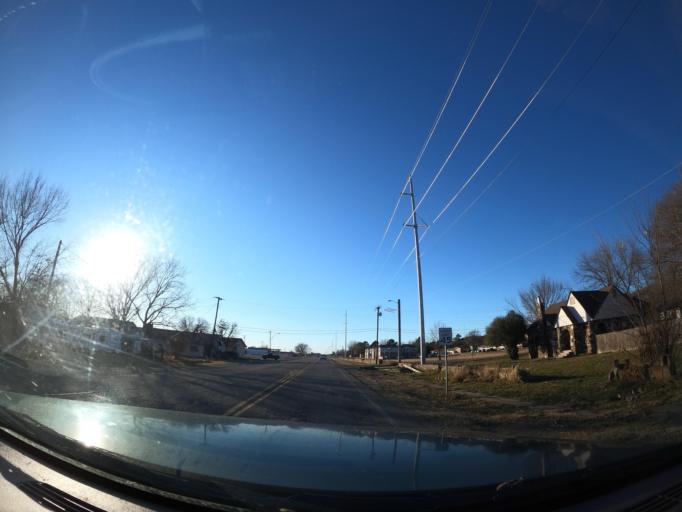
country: US
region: Oklahoma
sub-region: Latimer County
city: Wilburton
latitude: 34.9130
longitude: -95.3248
